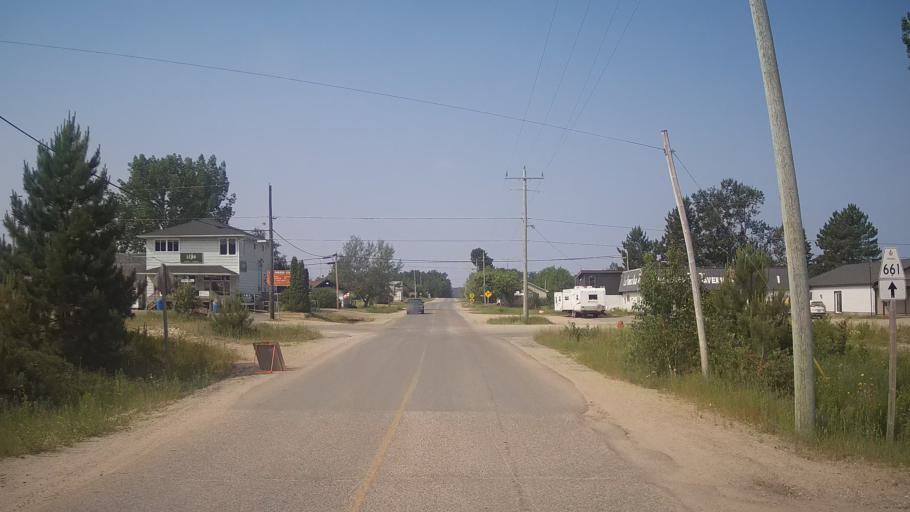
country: CA
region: Ontario
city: Timmins
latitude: 47.6751
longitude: -81.7227
